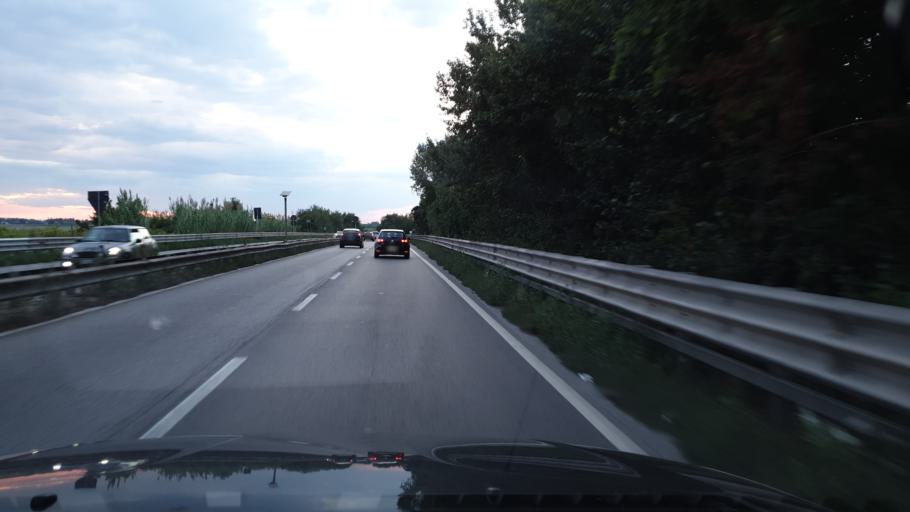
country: IT
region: Emilia-Romagna
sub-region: Provincia di Ravenna
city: Madonna Dell'Albero
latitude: 44.3849
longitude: 12.1935
